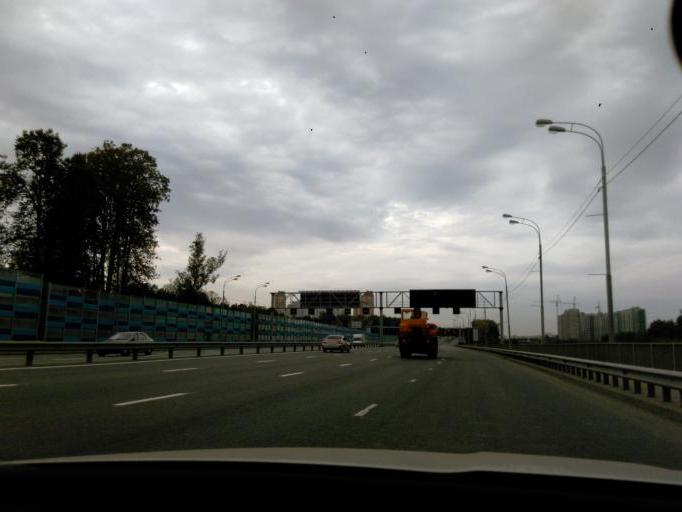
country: RU
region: Moscow
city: Severnyy
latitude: 55.9400
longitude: 37.5443
